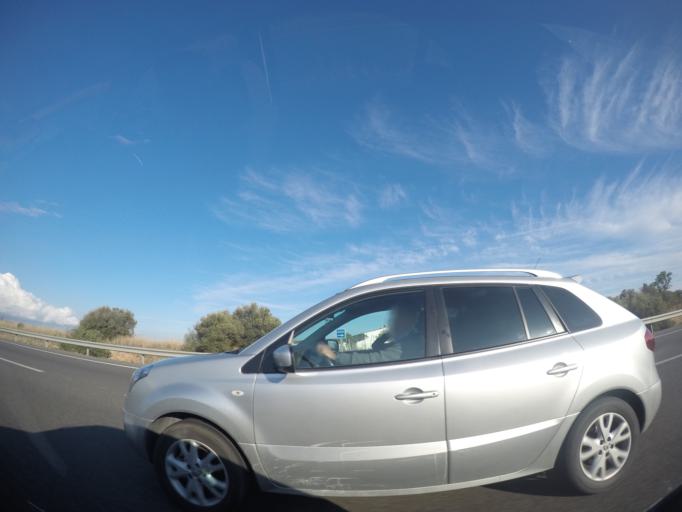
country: ES
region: Catalonia
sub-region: Provincia de Tarragona
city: Sant Jaume dels Domenys
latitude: 41.2929
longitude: 1.5979
